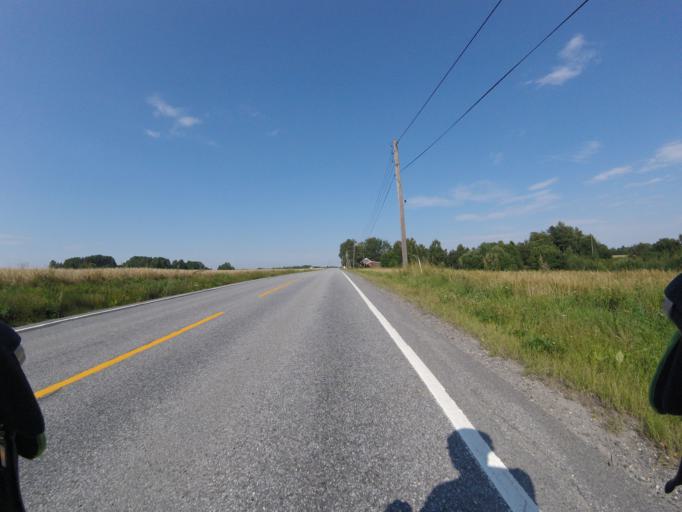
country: NO
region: Akershus
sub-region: Ullensaker
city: Klofta
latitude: 60.0547
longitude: 11.1178
